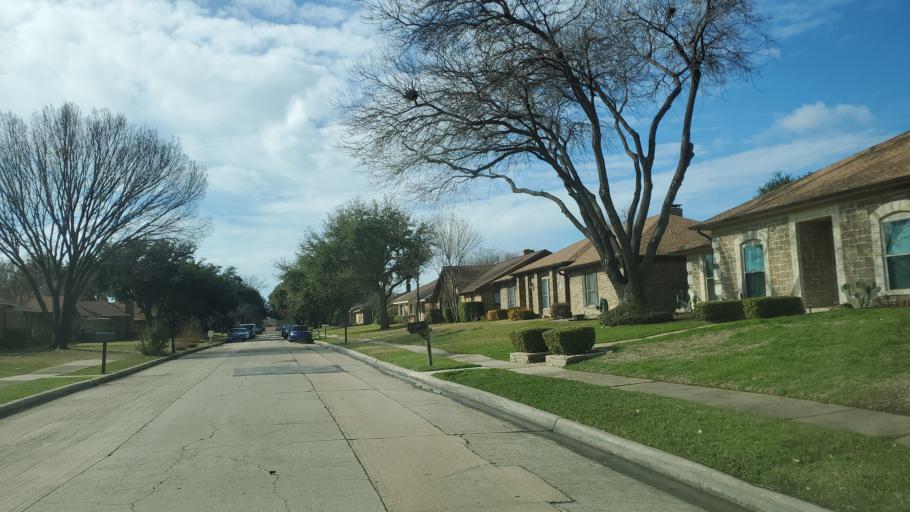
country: US
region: Texas
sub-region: Dallas County
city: Carrollton
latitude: 32.9795
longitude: -96.8793
